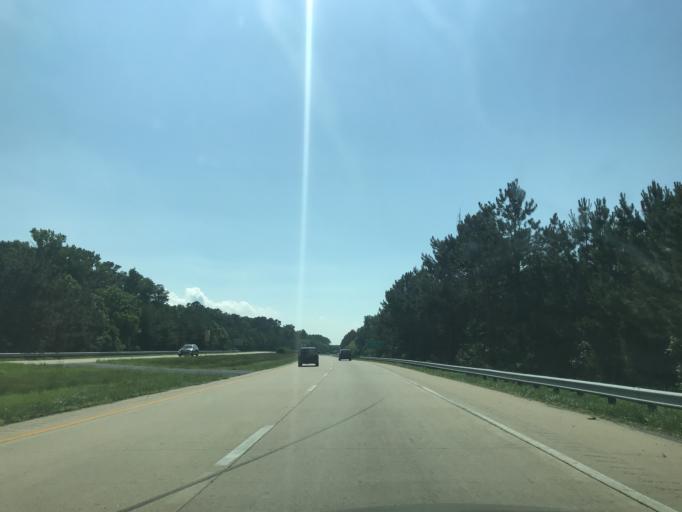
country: US
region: Maryland
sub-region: Wicomico County
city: Salisbury
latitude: 38.4047
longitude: -75.5952
